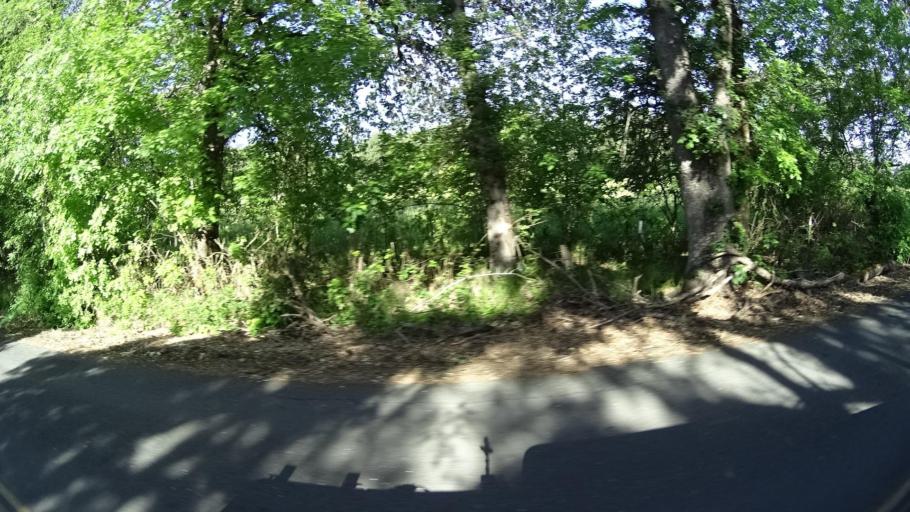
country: US
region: California
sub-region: Lake County
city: Kelseyville
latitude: 39.0216
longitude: -122.8475
